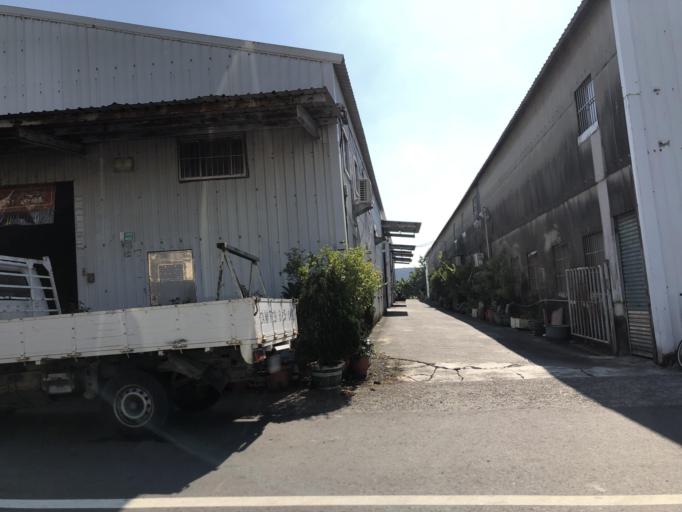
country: TW
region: Taiwan
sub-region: Tainan
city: Tainan
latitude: 23.0018
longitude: 120.2700
